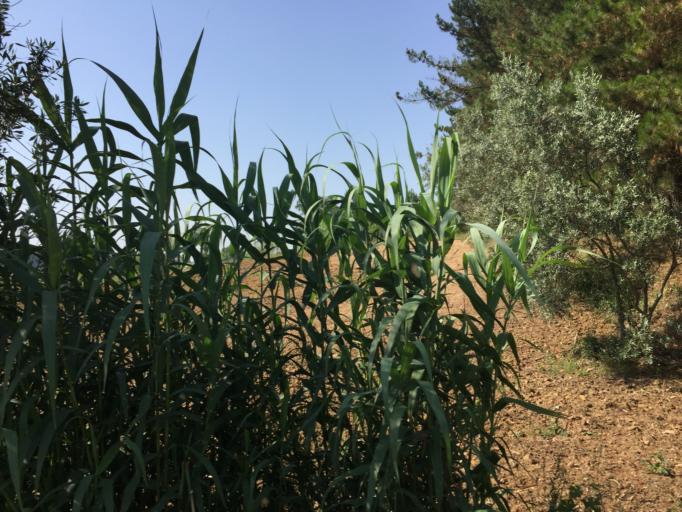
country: PT
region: Coimbra
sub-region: Cantanhede
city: Cantanhede
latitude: 40.4240
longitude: -8.5401
